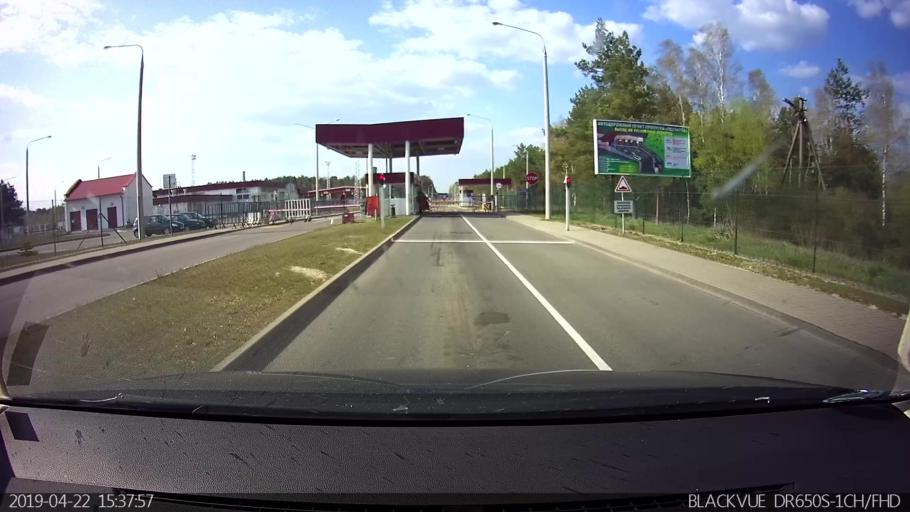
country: PL
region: Podlasie
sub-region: Powiat hajnowski
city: Czeremcha
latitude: 52.4647
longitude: 23.3614
